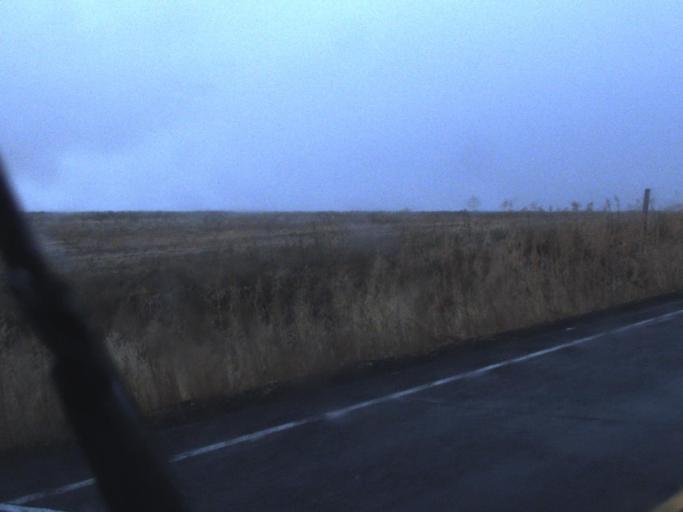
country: US
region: Washington
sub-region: Lincoln County
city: Davenport
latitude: 47.3478
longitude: -118.0860
